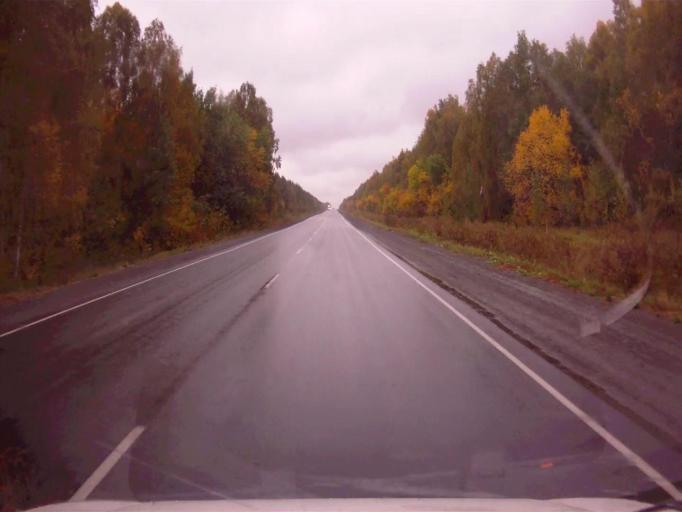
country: RU
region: Chelyabinsk
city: Roshchino
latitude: 55.3740
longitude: 61.1537
